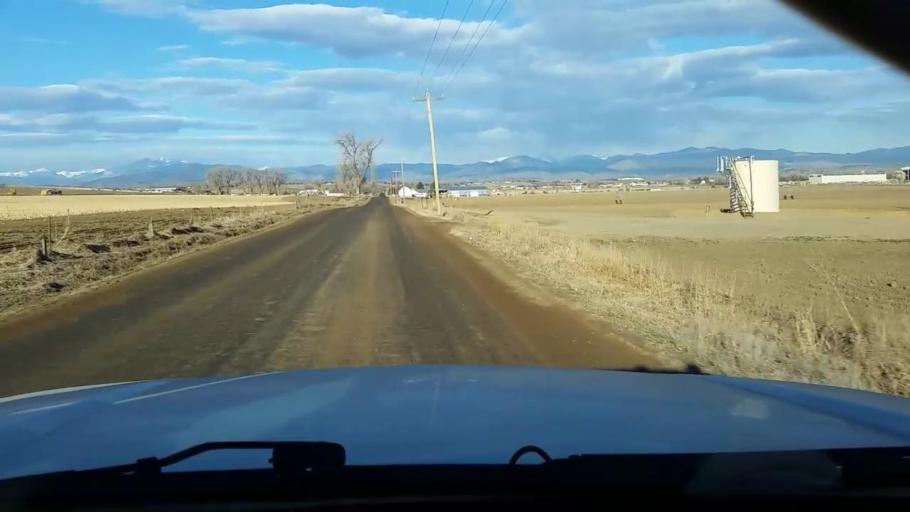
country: US
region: Colorado
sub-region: Larimer County
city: Campion
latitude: 40.3710
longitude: -105.0421
